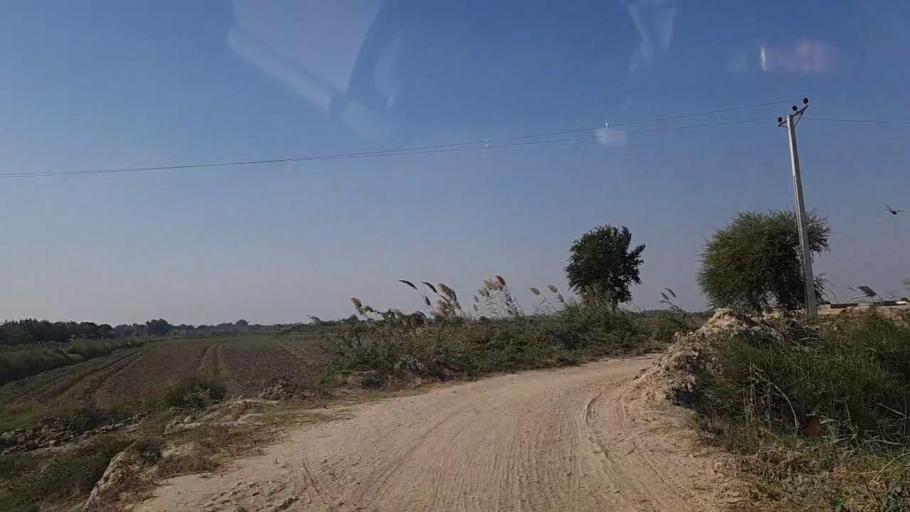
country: PK
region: Sindh
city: Thatta
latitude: 24.7682
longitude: 67.9326
